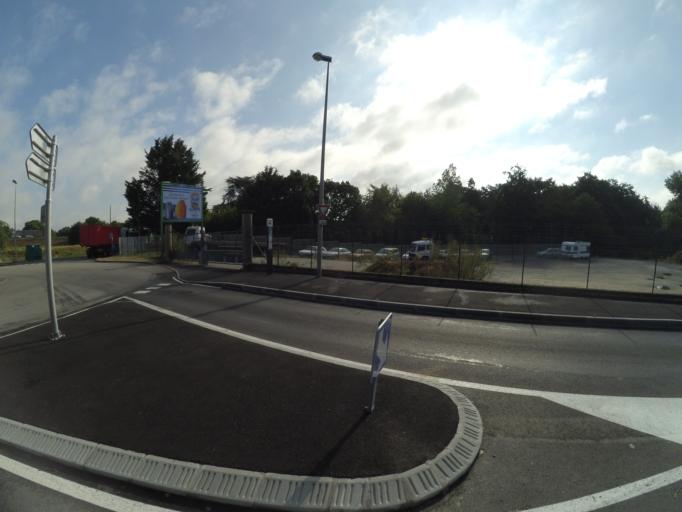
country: FR
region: Brittany
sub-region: Departement du Morbihan
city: Vannes
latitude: 47.6687
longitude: -2.7451
